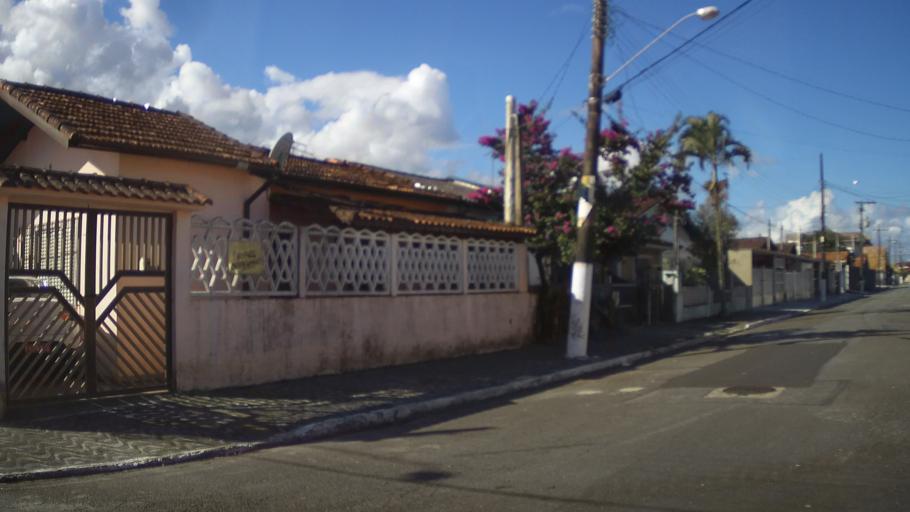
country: BR
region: Sao Paulo
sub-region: Mongagua
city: Mongagua
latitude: -24.0603
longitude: -46.5531
